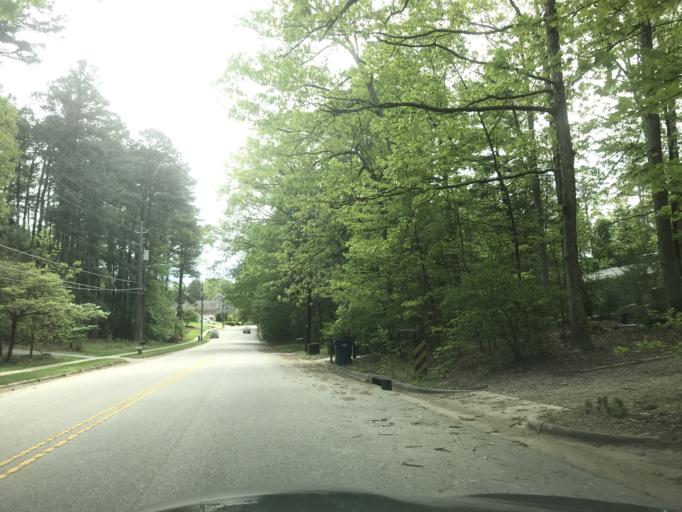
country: US
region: North Carolina
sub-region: Wake County
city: West Raleigh
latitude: 35.7813
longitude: -78.7128
